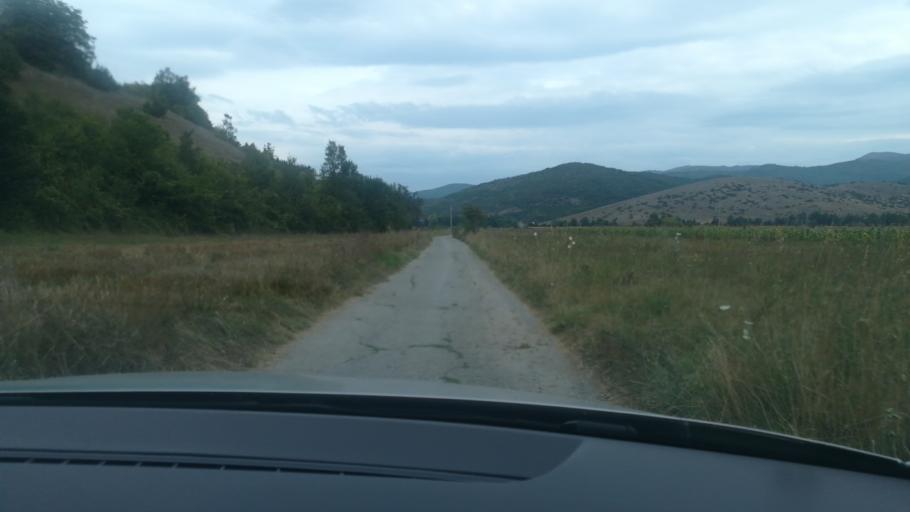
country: MK
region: Debarca
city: Belcista
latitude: 41.2891
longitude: 20.8305
